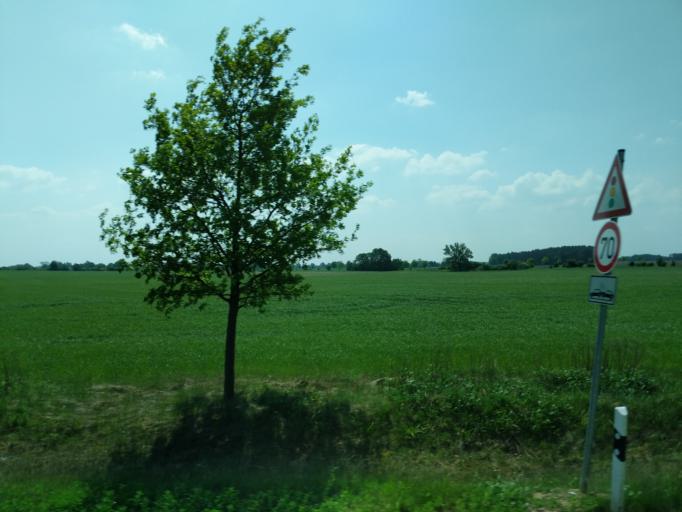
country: DE
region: Mecklenburg-Vorpommern
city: Klein Rogahn
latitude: 53.5611
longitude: 11.3497
